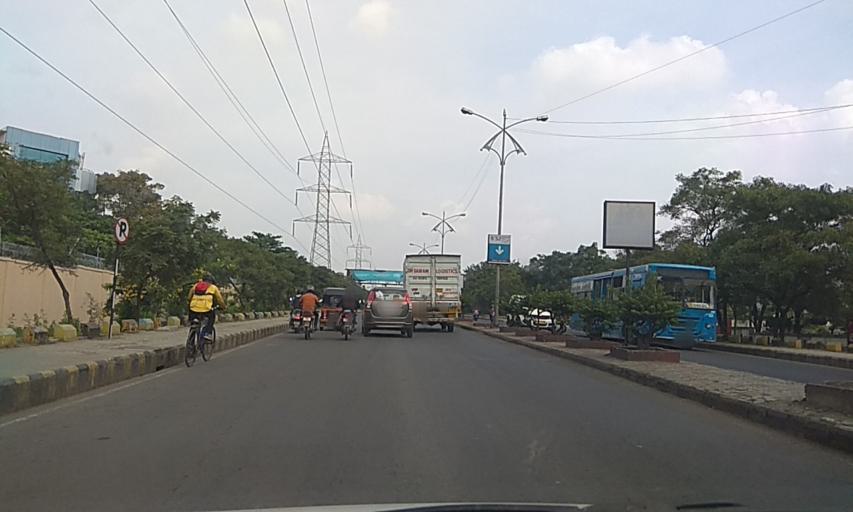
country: IN
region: Maharashtra
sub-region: Pune Division
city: Pimpri
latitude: 18.5938
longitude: 73.7085
